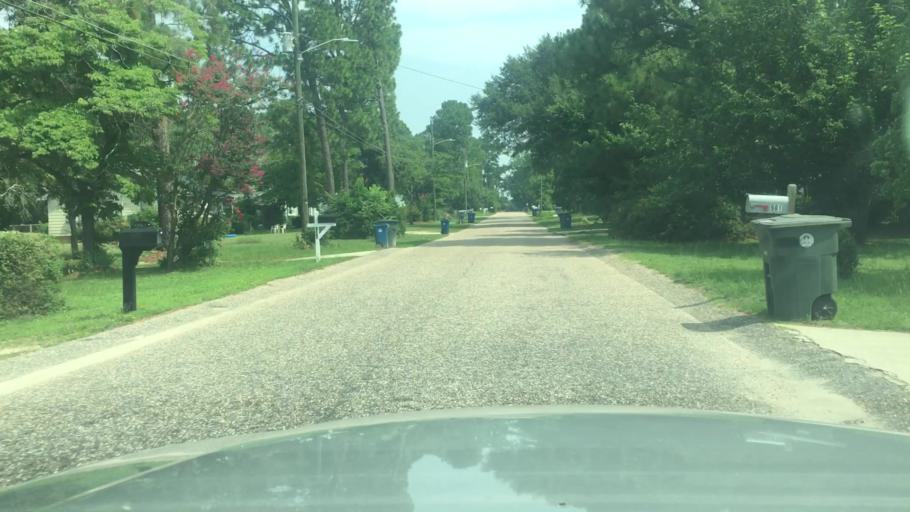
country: US
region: North Carolina
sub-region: Cumberland County
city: Hope Mills
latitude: 35.0348
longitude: -78.9432
